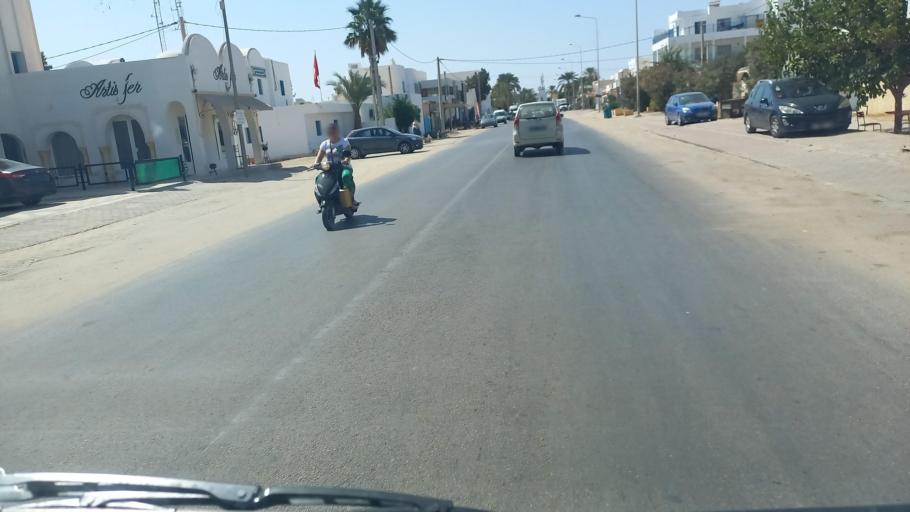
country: TN
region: Madanin
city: Houmt Souk
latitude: 33.8759
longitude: 10.8744
